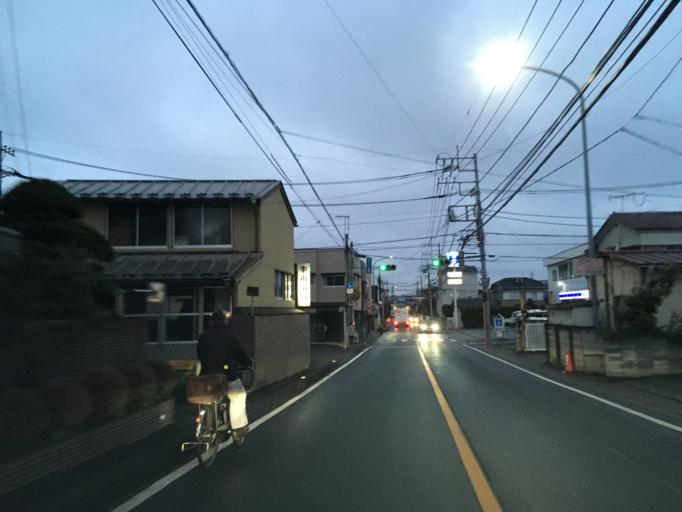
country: JP
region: Saitama
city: Asaka
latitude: 35.7917
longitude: 139.5839
